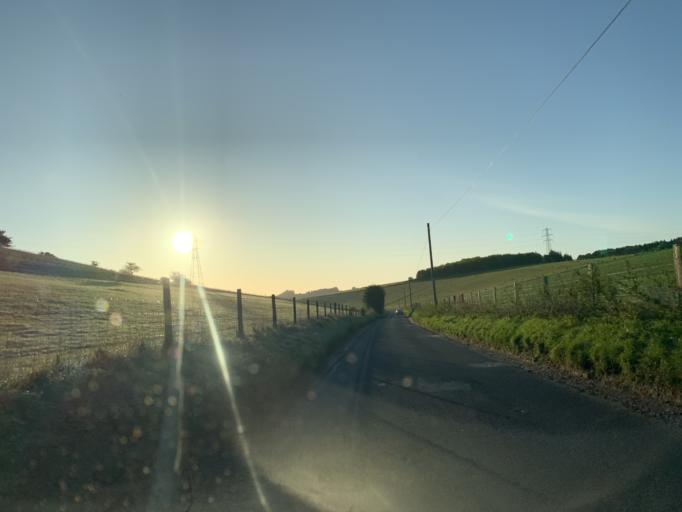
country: GB
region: England
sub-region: Wiltshire
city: Woodford
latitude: 51.1255
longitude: -1.8416
